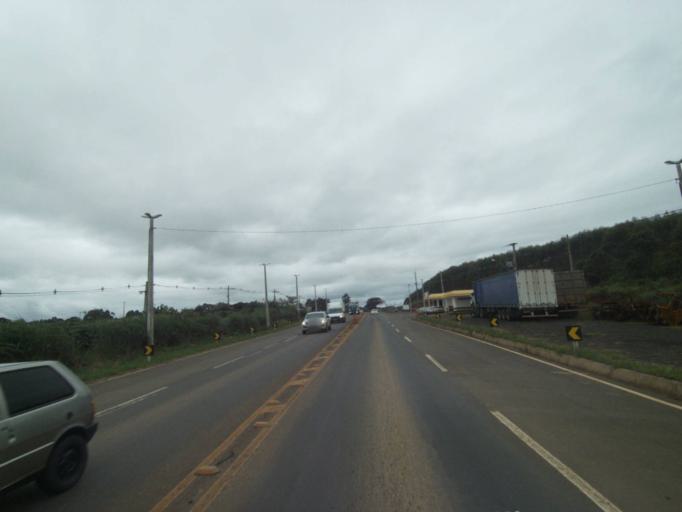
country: BR
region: Parana
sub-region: Telemaco Borba
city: Telemaco Borba
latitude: -24.3867
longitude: -50.6810
